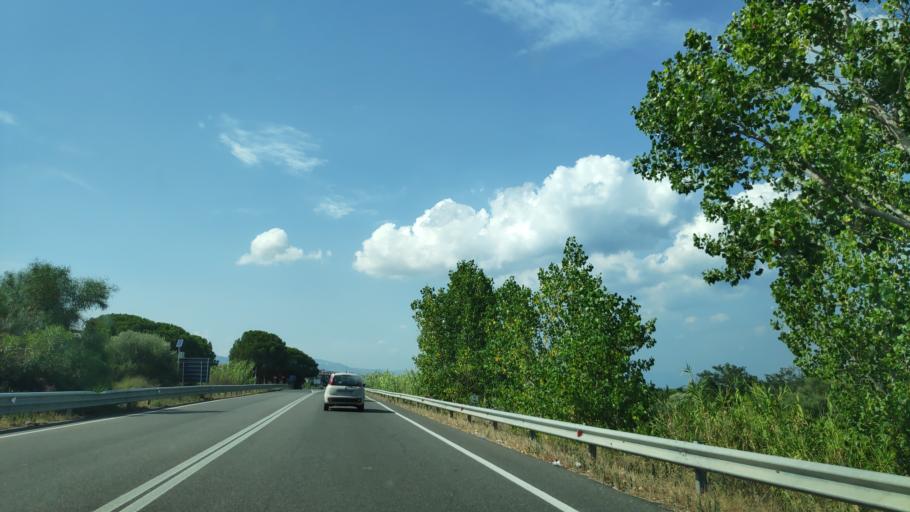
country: IT
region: Calabria
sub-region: Provincia di Catanzaro
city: Isca Marina
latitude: 38.6082
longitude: 16.5558
